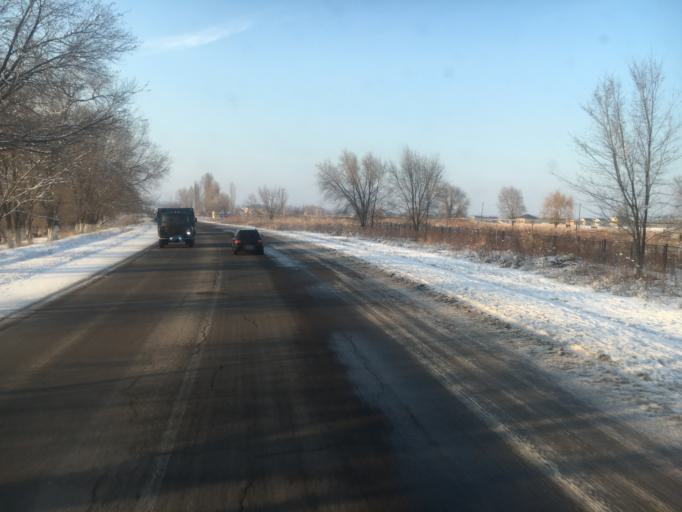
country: KZ
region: Almaty Oblysy
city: Burunday
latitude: 43.3411
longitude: 76.6584
